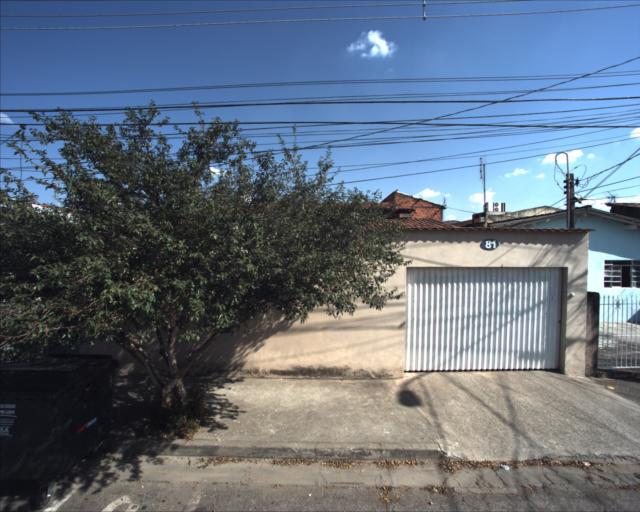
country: BR
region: Sao Paulo
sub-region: Sorocaba
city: Sorocaba
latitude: -23.4689
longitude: -47.4425
